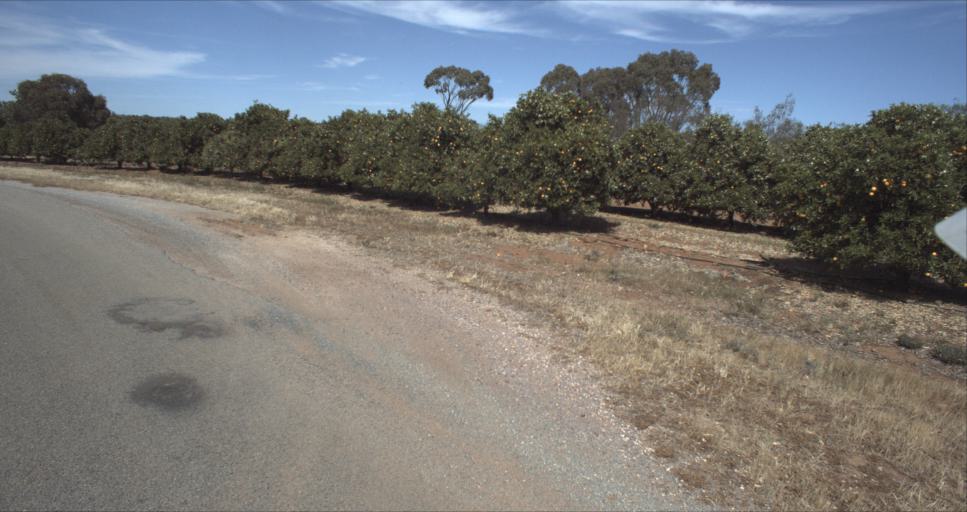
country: AU
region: New South Wales
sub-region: Leeton
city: Leeton
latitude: -34.5872
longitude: 146.4612
